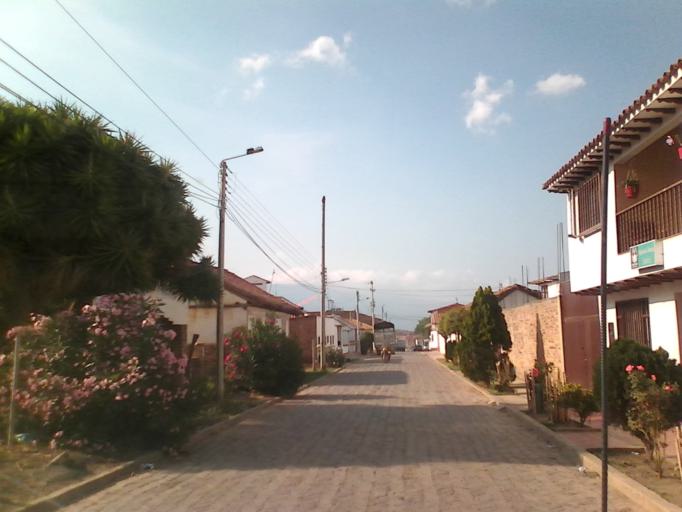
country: CO
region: Boyaca
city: Sachica
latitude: 5.5824
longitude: -73.5417
